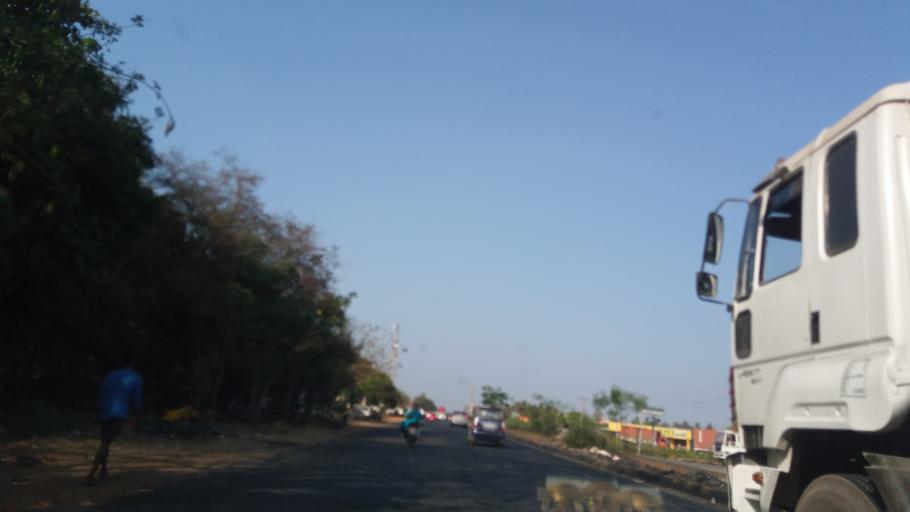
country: IN
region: Tamil Nadu
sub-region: Kancheepuram
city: Nandambakkam
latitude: 13.0276
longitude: 80.0286
